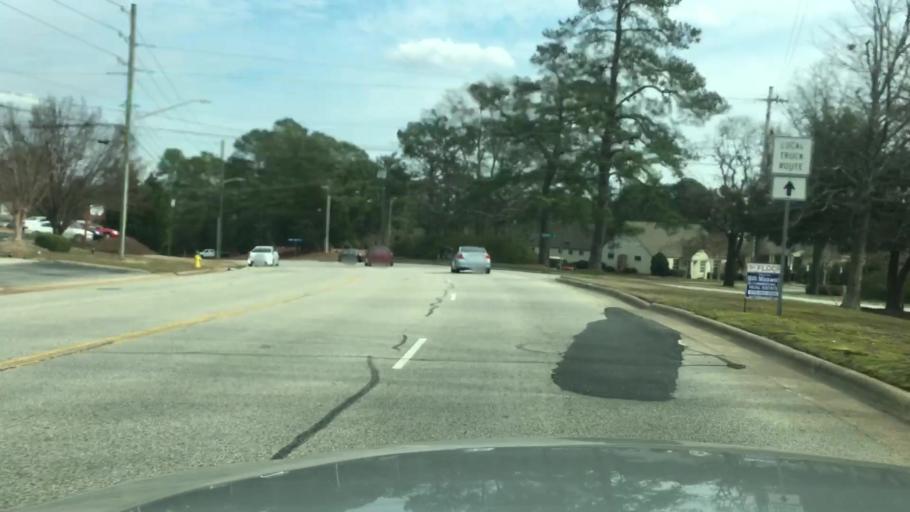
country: US
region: North Carolina
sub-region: Cumberland County
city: Fayetteville
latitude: 35.0462
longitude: -78.9181
